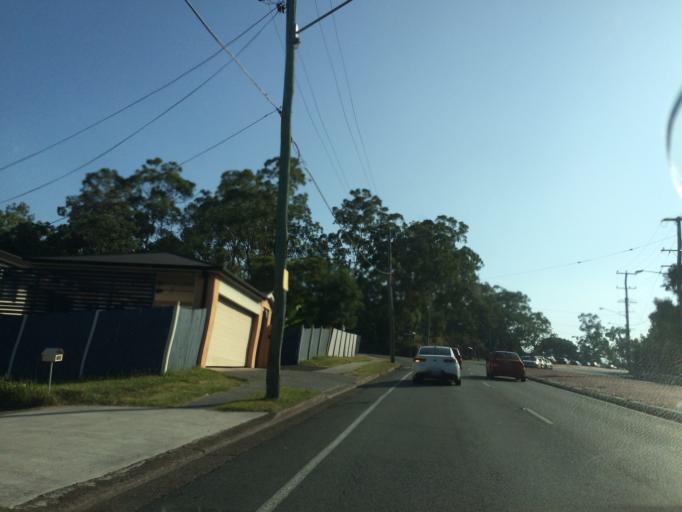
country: AU
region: Queensland
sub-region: Brisbane
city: Kenmore Hills
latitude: -27.5081
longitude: 152.9556
